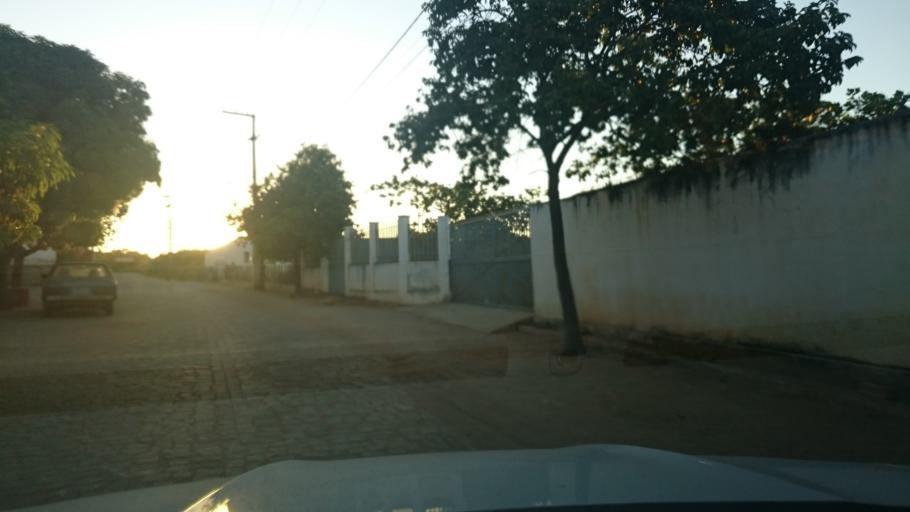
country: BR
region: Rio Grande do Norte
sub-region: Umarizal
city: Umarizal
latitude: -6.0225
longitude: -37.9935
